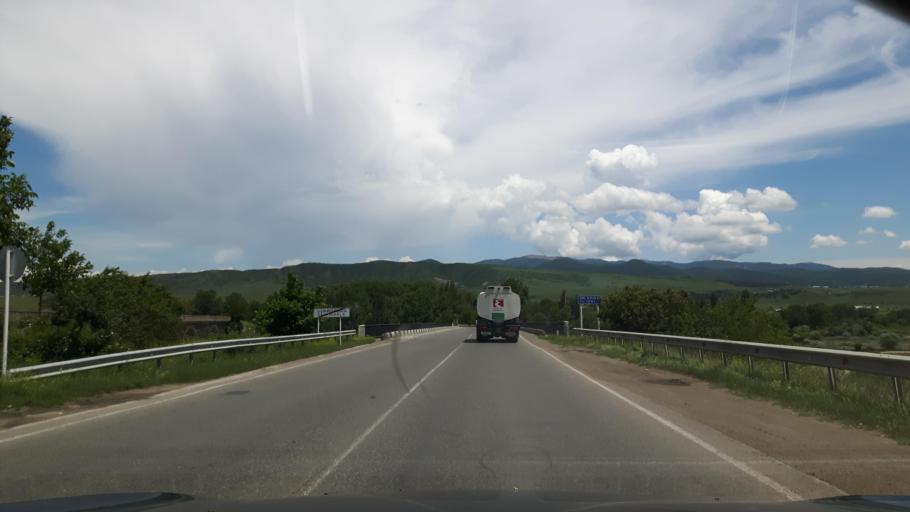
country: GE
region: Kakheti
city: Sagarejo
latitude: 41.7216
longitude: 45.1791
